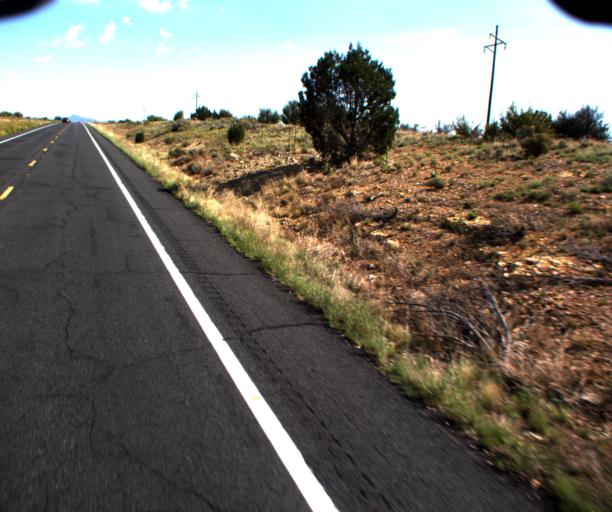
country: US
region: Arizona
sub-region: Coconino County
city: Williams
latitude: 35.5883
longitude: -112.1504
